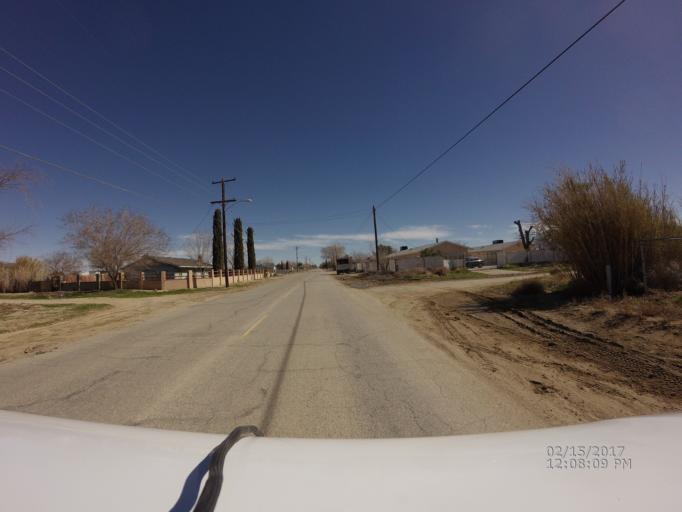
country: US
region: California
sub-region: Los Angeles County
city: Littlerock
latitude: 34.5742
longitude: -117.9656
